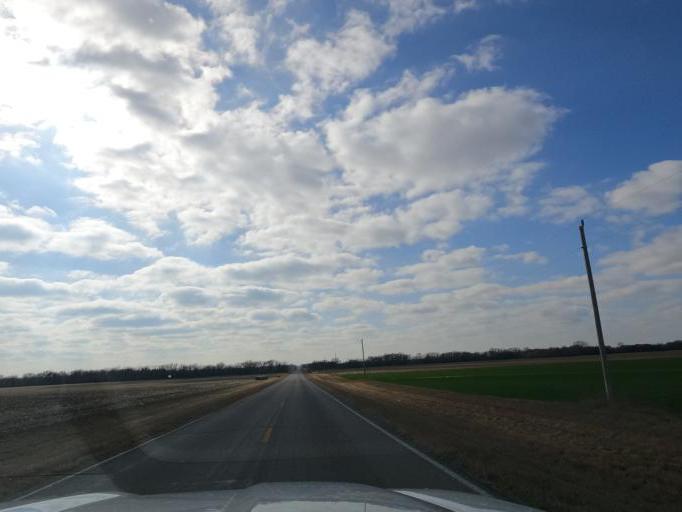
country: US
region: Kansas
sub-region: McPherson County
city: Inman
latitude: 38.2322
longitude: -97.8556
